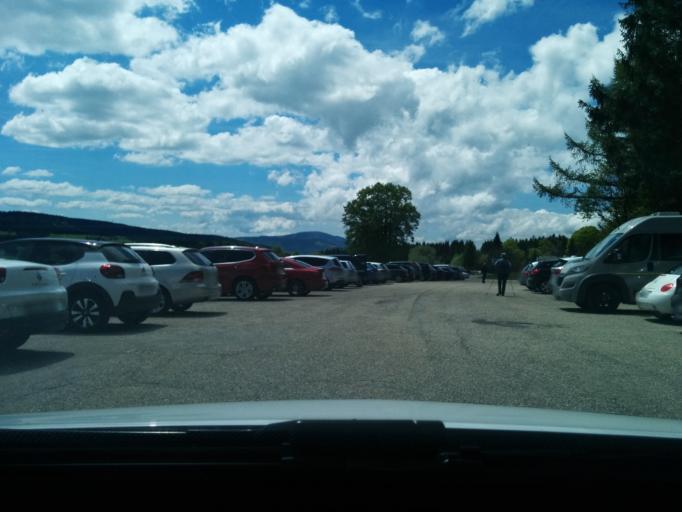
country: DE
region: Baden-Wuerttemberg
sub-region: Freiburg Region
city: Horben
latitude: 47.9059
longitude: 7.8897
